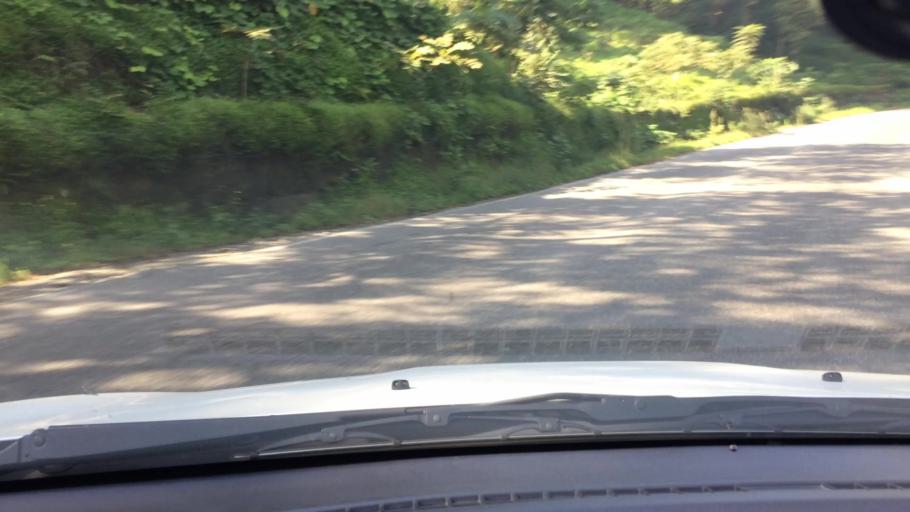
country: GE
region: Ajaria
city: Kobuleti
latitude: 41.7645
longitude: 41.7551
